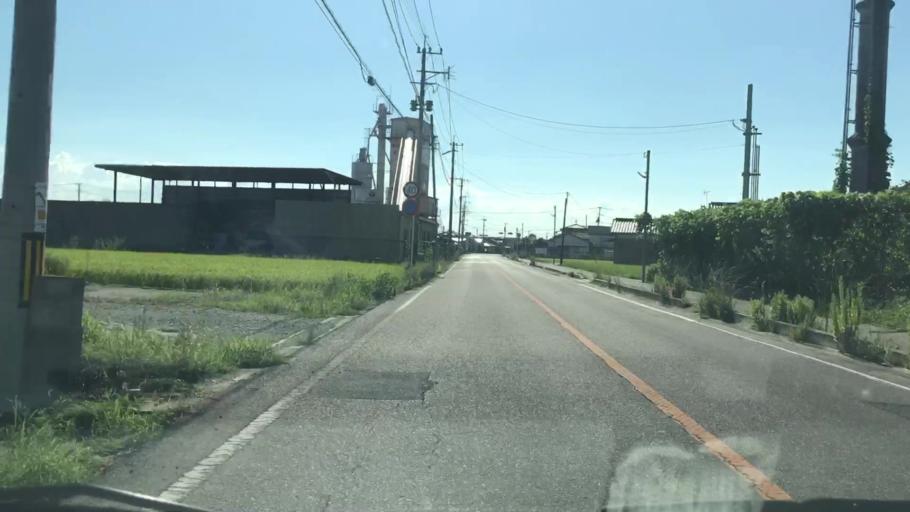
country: JP
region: Saga Prefecture
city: Okawa
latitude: 33.1899
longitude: 130.3283
